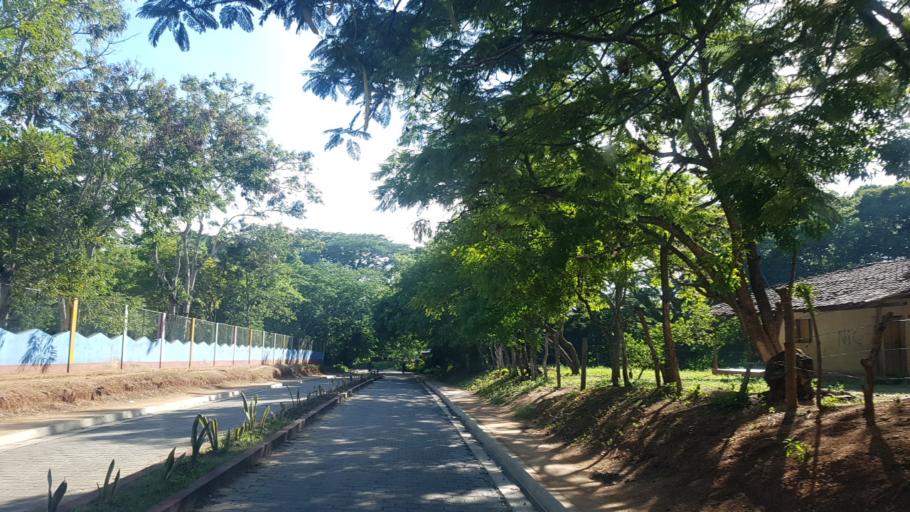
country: NI
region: Nueva Segovia
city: Mozonte
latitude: 13.6577
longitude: -86.4393
